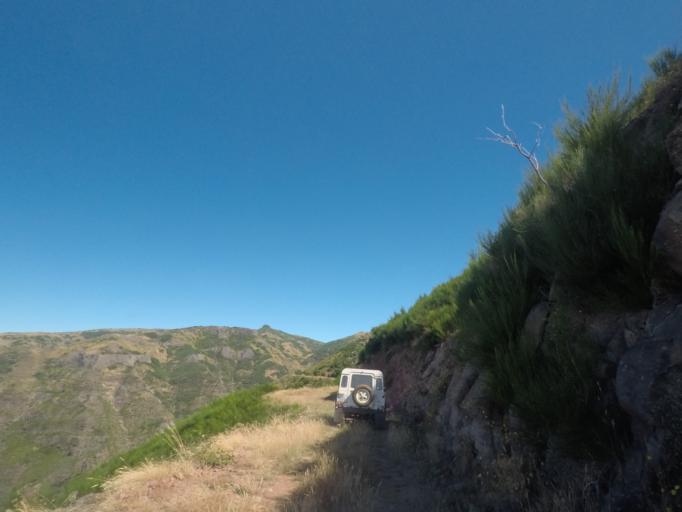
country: PT
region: Madeira
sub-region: Funchal
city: Nossa Senhora do Monte
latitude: 32.7051
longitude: -16.9161
